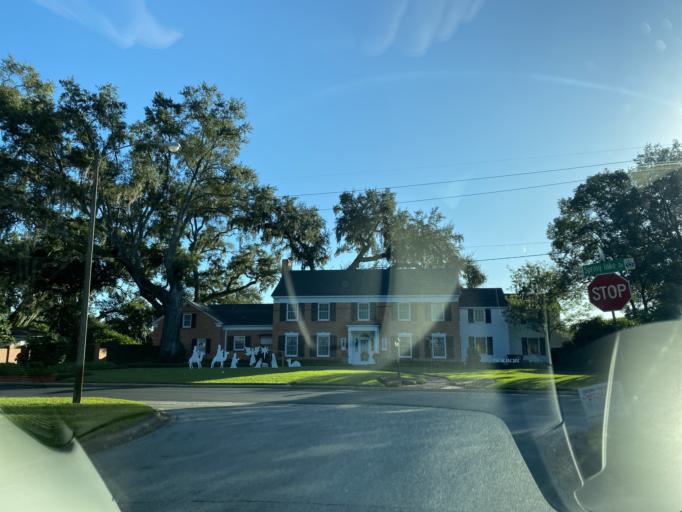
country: US
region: Florida
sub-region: Orange County
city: Orlando
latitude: 28.5561
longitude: -81.4023
